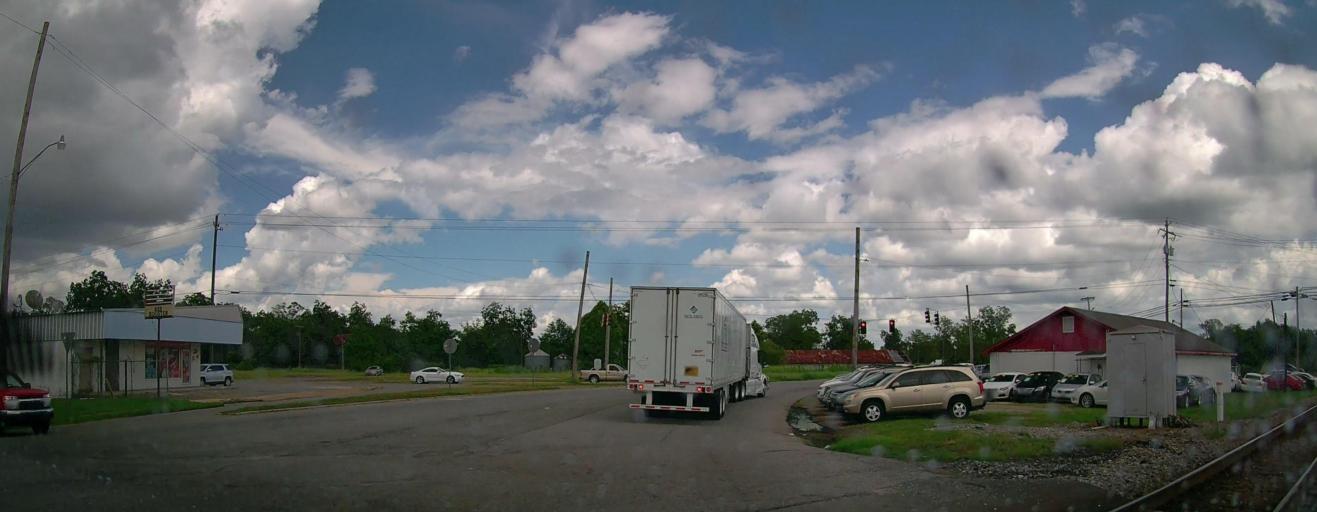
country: US
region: Georgia
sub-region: Ben Hill County
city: Fitzgerald
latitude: 31.7150
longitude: -83.2448
